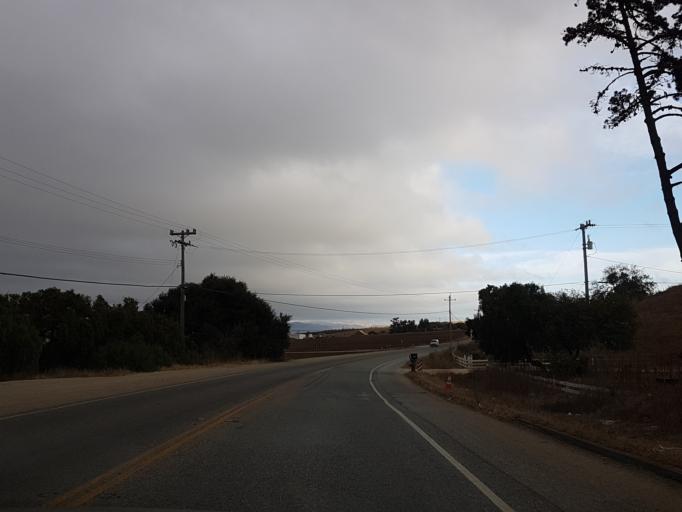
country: US
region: California
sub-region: Monterey County
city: Salinas
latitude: 36.5964
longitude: -121.6220
